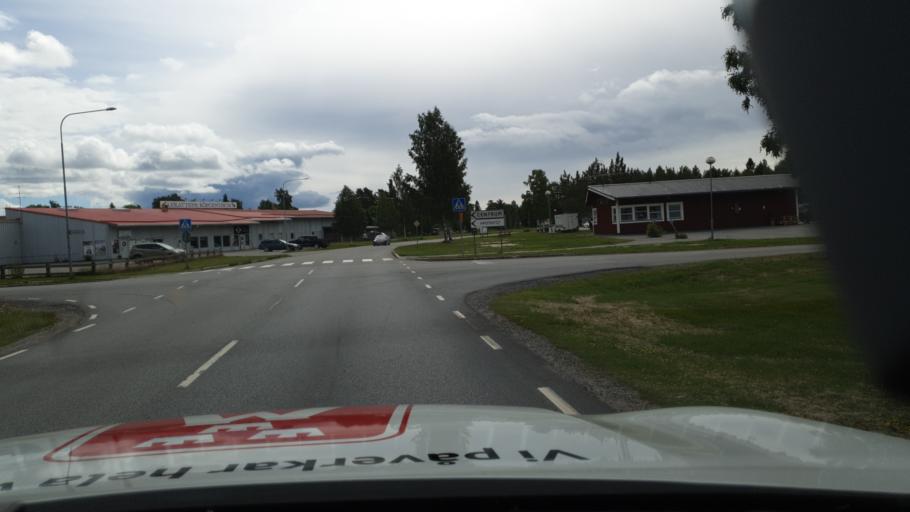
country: SE
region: Vaesterbotten
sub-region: Nordmalings Kommun
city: Nordmaling
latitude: 63.5685
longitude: 19.4936
